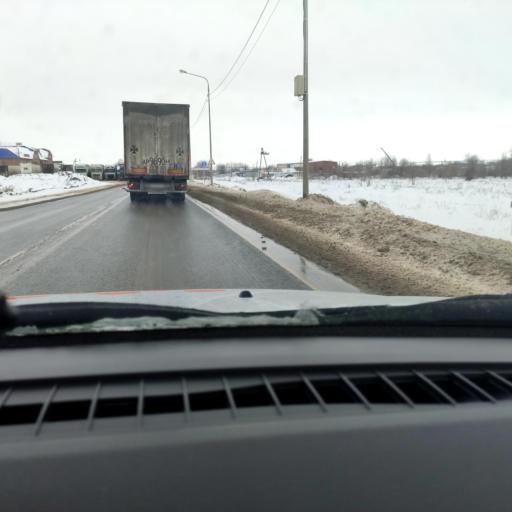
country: RU
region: Samara
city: Dubovyy Umet
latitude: 52.8280
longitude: 50.4975
